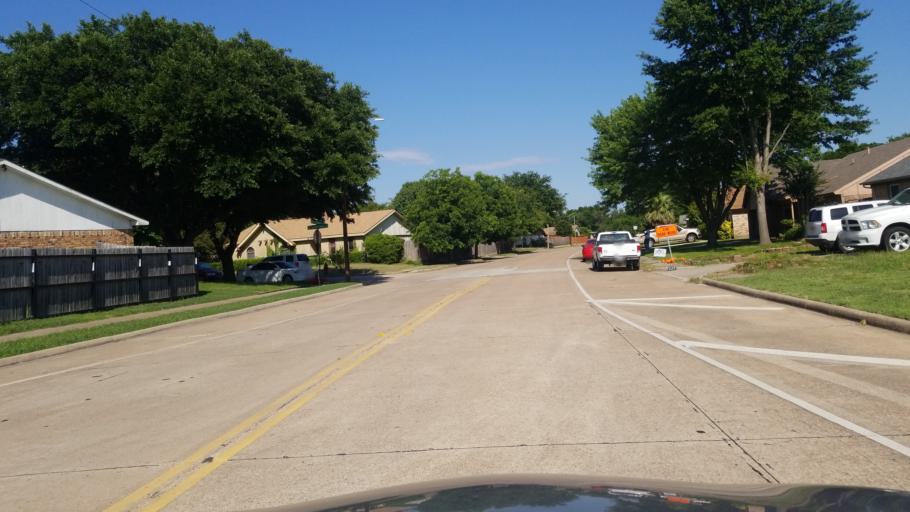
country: US
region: Texas
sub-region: Dallas County
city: Grand Prairie
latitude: 32.6811
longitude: -97.0175
